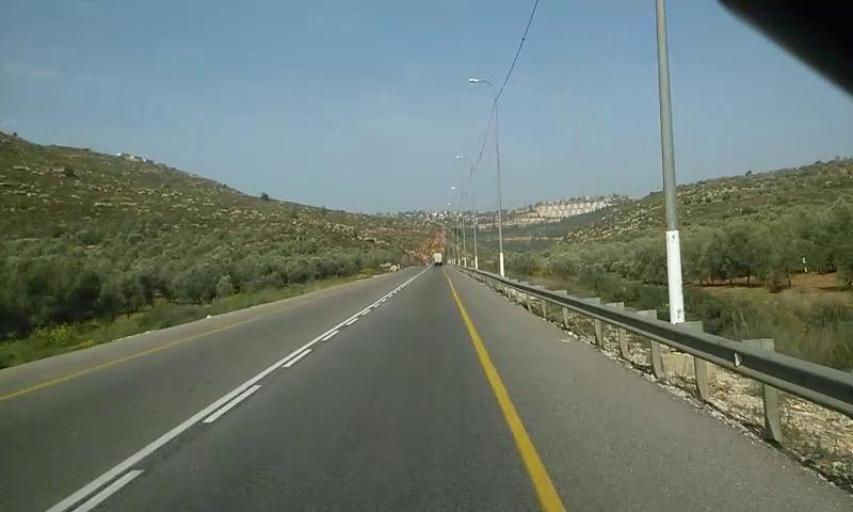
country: PS
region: West Bank
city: Qaryut
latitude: 32.0626
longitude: 35.2774
